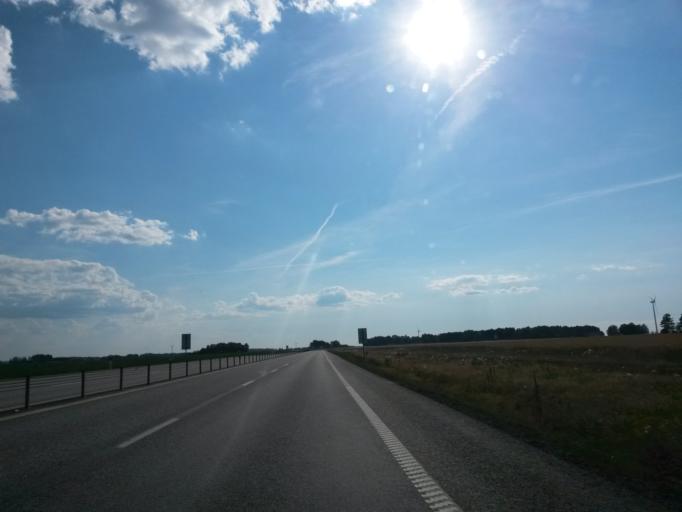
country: SE
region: Vaestra Goetaland
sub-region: Vara Kommun
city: Kvanum
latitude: 58.3151
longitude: 13.1098
